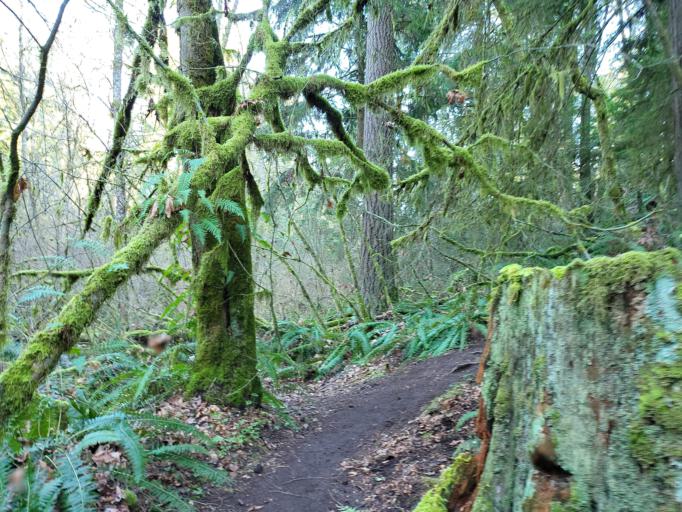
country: US
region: Washington
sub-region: King County
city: East Renton Highlands
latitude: 47.5135
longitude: -122.1212
